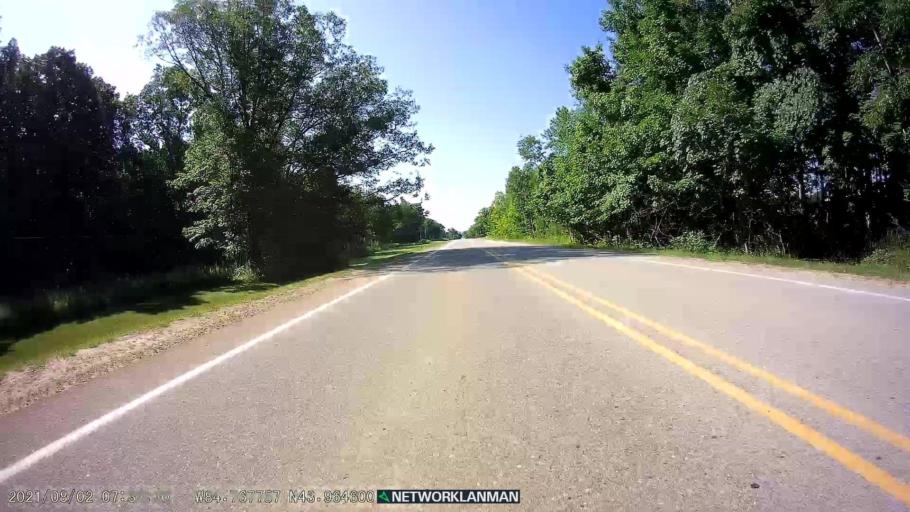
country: US
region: Michigan
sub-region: Clare County
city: Harrison
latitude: 43.9650
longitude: -84.7678
